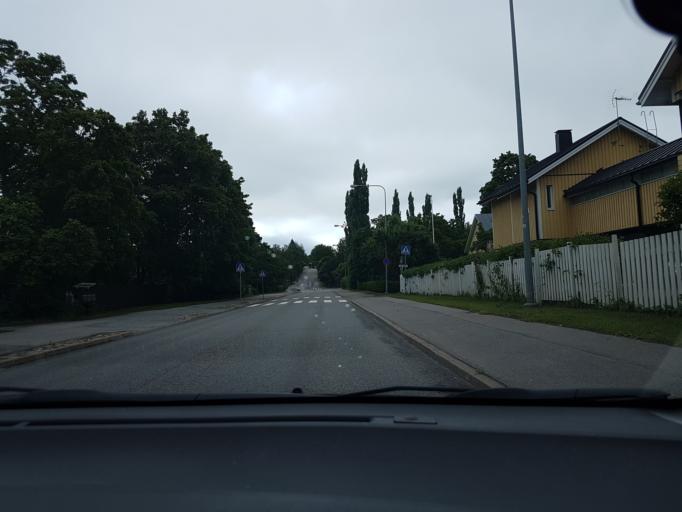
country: FI
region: Uusimaa
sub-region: Helsinki
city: Vantaa
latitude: 60.2730
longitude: 25.0448
